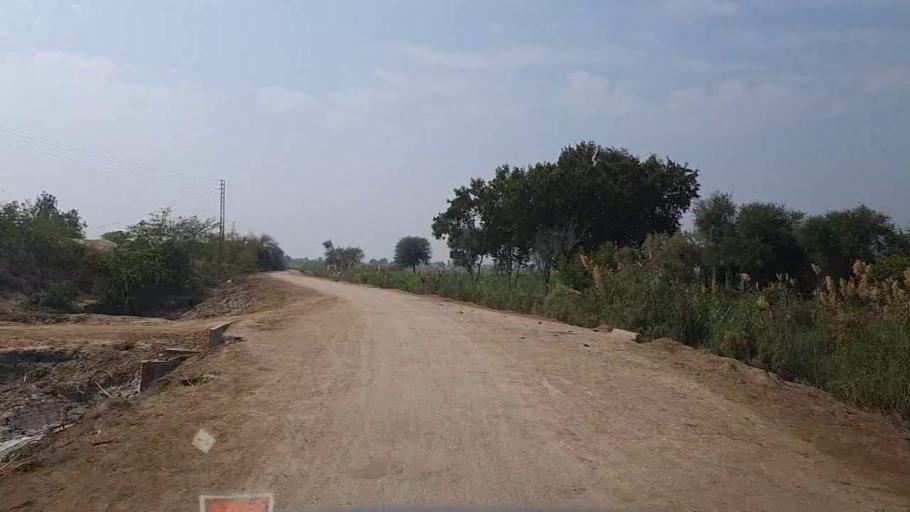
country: PK
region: Sindh
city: Mirwah Gorchani
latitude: 25.3486
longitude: 69.0873
